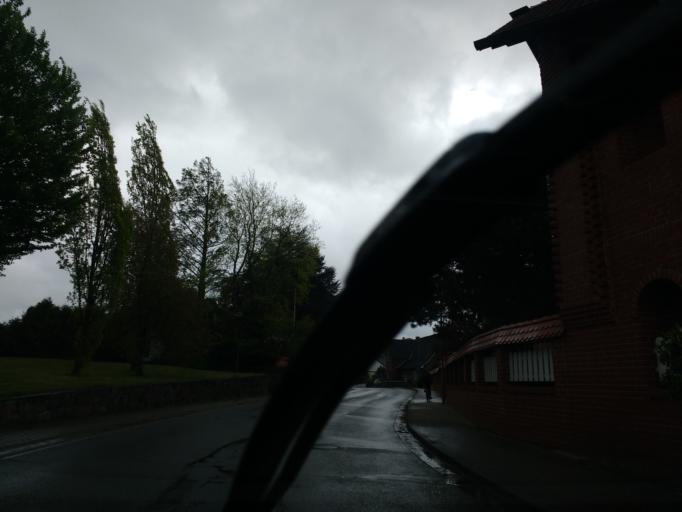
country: DE
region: Schleswig-Holstein
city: Loose
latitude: 54.5204
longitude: 9.8865
